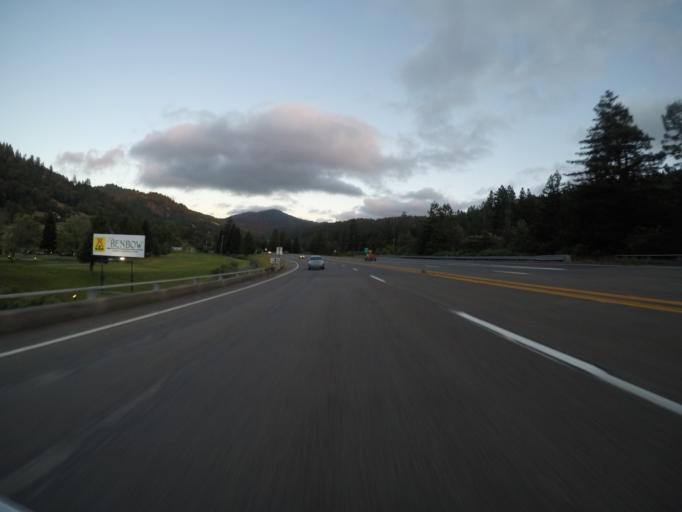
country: US
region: California
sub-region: Humboldt County
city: Redway
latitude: 40.0675
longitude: -123.7885
